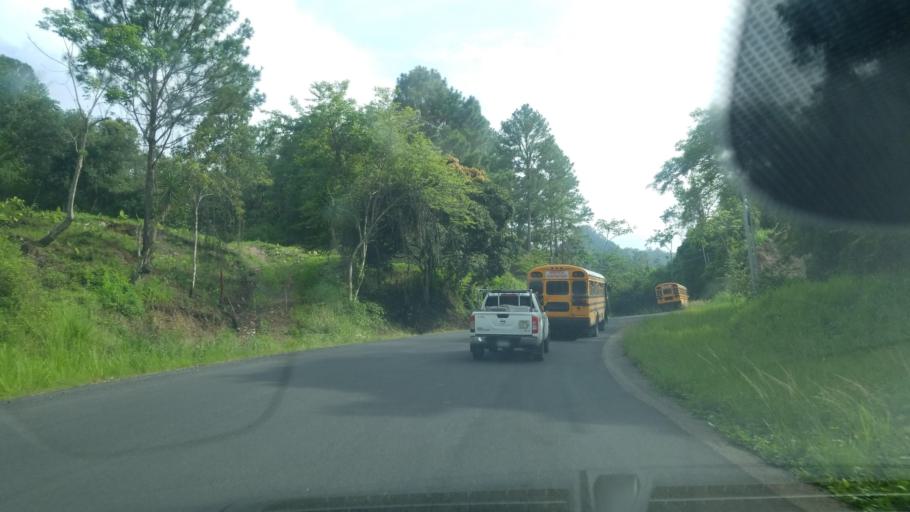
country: HN
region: Santa Barbara
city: Trinidad
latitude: 15.1932
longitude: -88.2732
